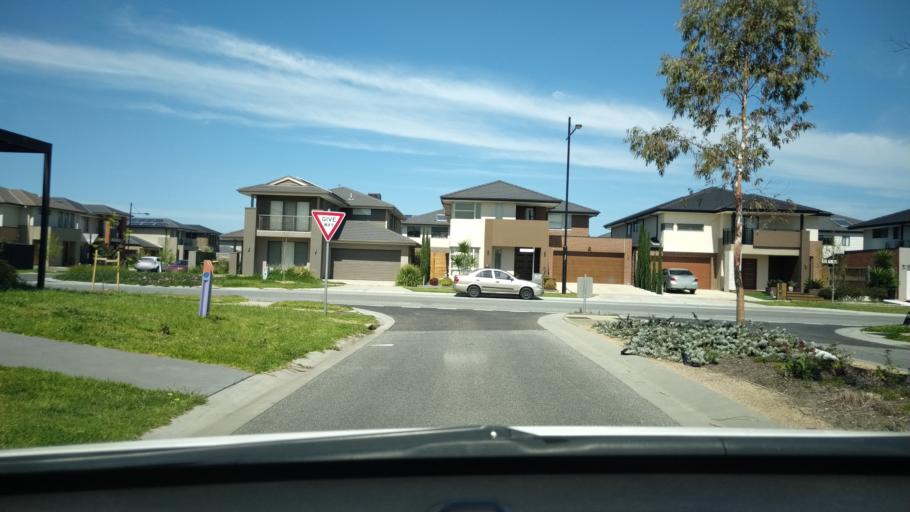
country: AU
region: Victoria
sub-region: Greater Dandenong
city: Keysborough
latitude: -38.0014
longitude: 145.1722
